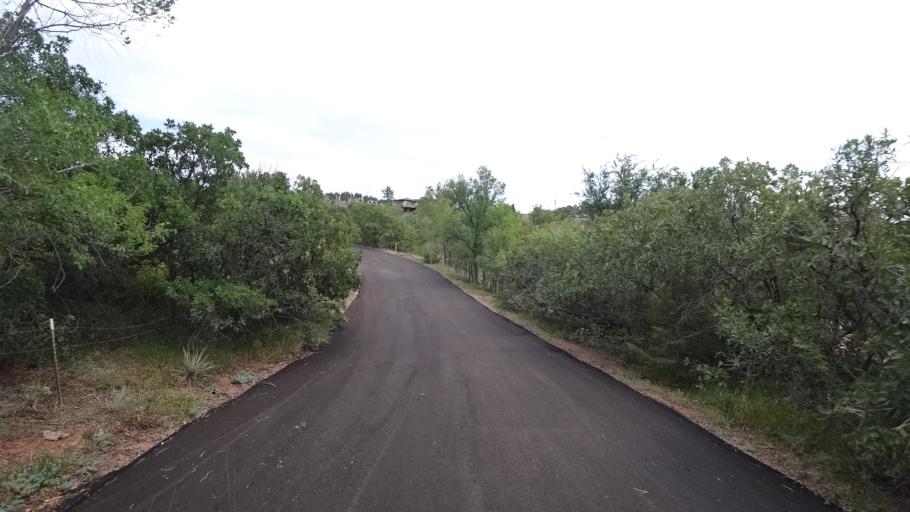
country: US
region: Colorado
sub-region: El Paso County
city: Manitou Springs
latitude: 38.8619
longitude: -104.8761
